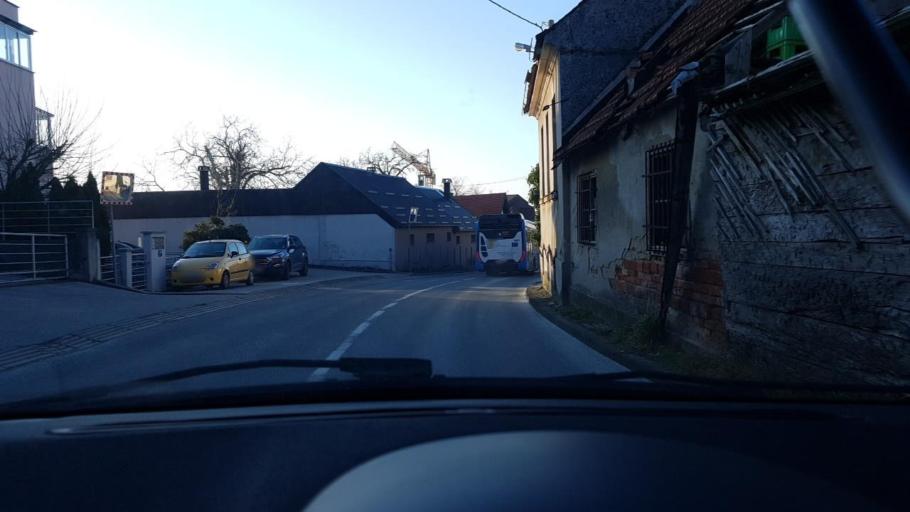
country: HR
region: Grad Zagreb
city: Zagreb
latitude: 45.8473
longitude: 15.9977
